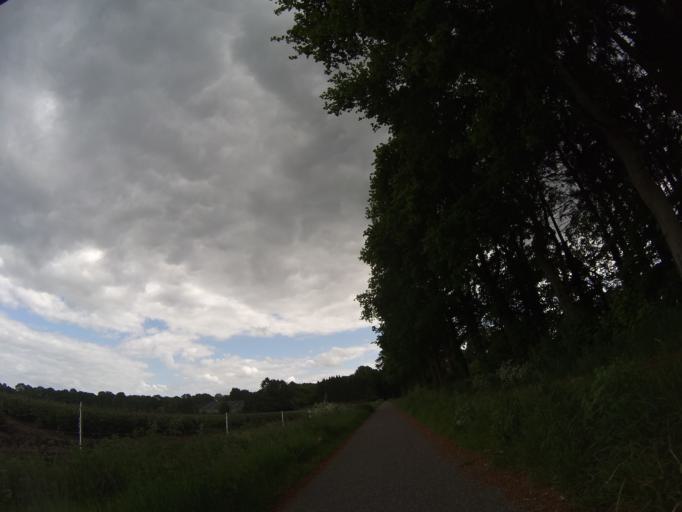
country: NL
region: Drenthe
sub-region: Gemeente Emmen
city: Emmen
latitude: 52.8453
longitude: 6.8753
